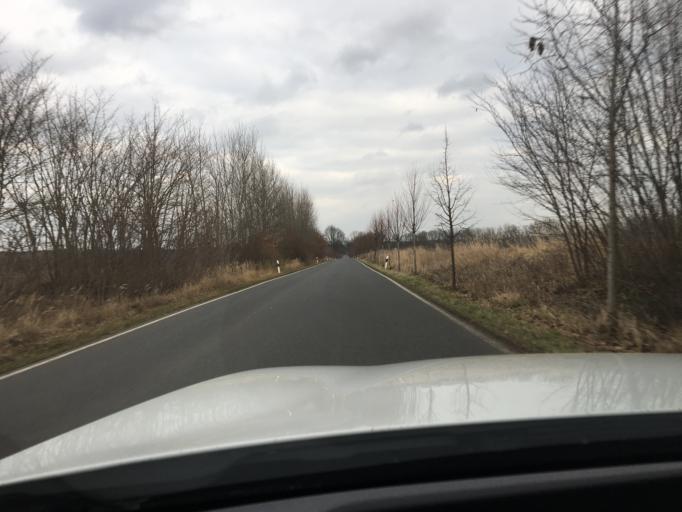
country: DE
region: Brandenburg
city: Liebenwalde
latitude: 52.8829
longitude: 13.4568
